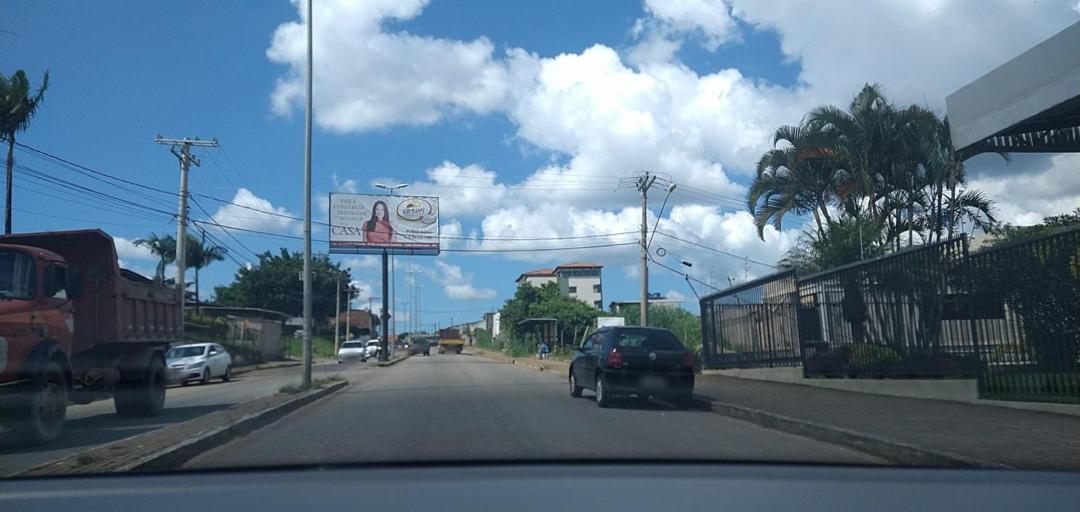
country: BR
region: Minas Gerais
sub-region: Joao Monlevade
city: Joao Monlevade
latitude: -19.8344
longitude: -43.1901
